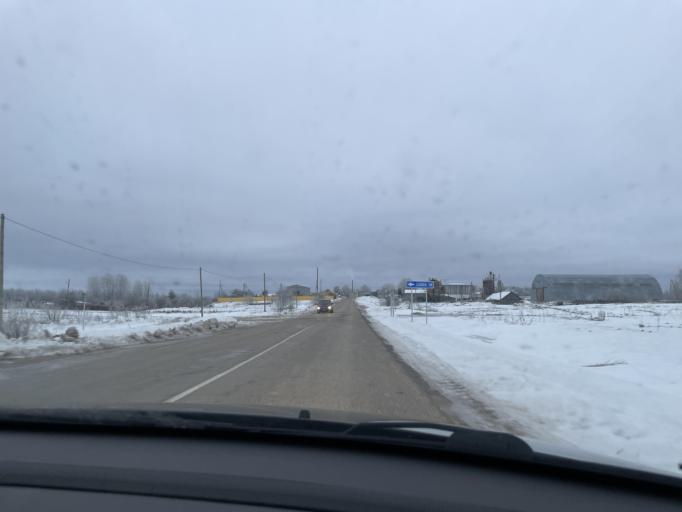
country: LV
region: Ludzas Rajons
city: Ludza
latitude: 56.4362
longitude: 27.5402
